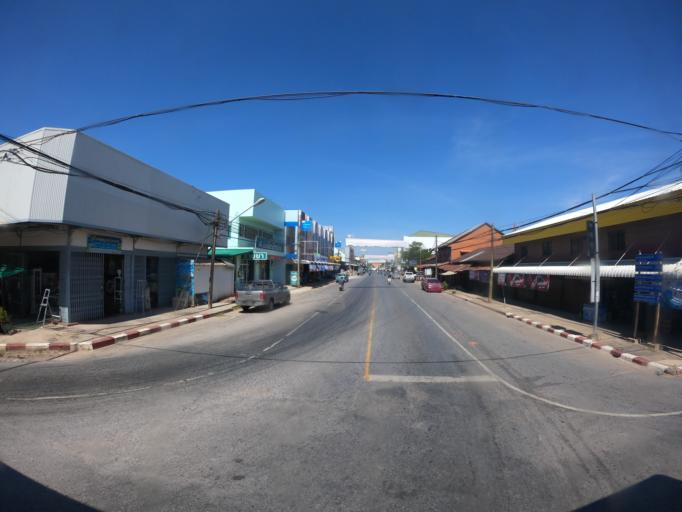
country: TH
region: Khon Kaen
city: Ban Phai
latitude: 16.0566
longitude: 102.7254
